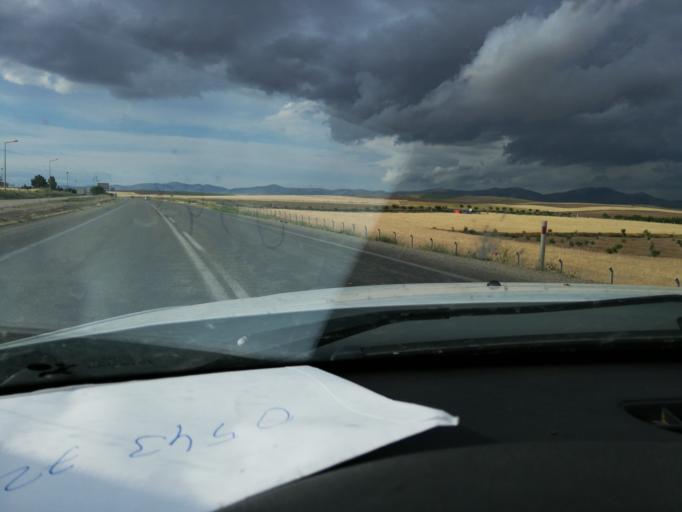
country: TR
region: Kirsehir
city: Kirsehir
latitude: 39.0406
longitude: 34.1764
